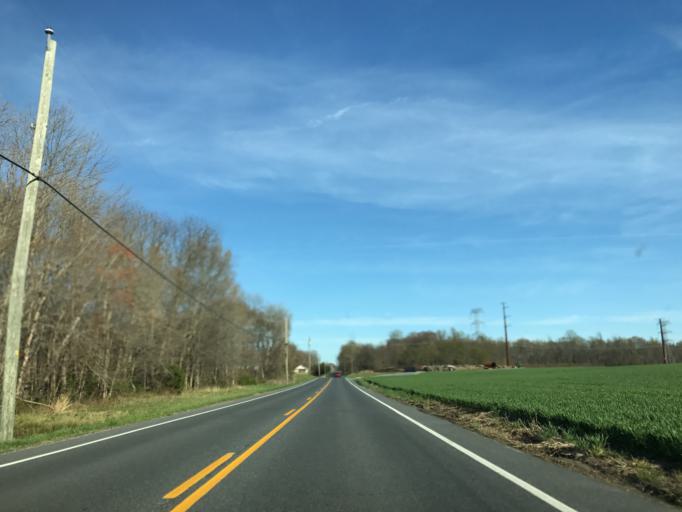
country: US
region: Maryland
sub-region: Caroline County
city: Greensboro
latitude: 39.0356
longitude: -75.7780
